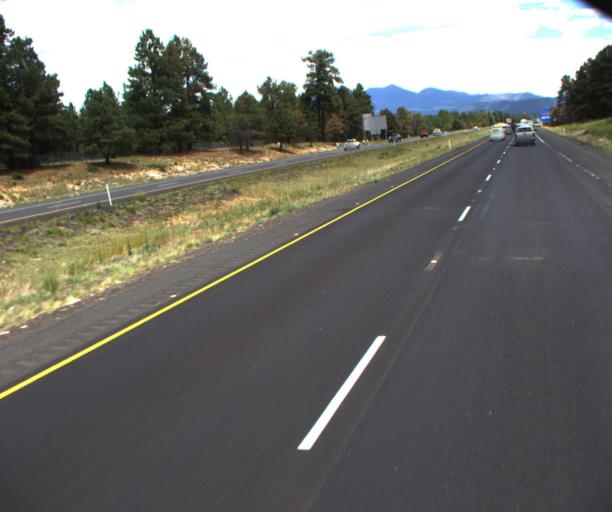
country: US
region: Arizona
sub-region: Coconino County
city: Kachina Village
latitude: 35.1484
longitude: -111.6821
